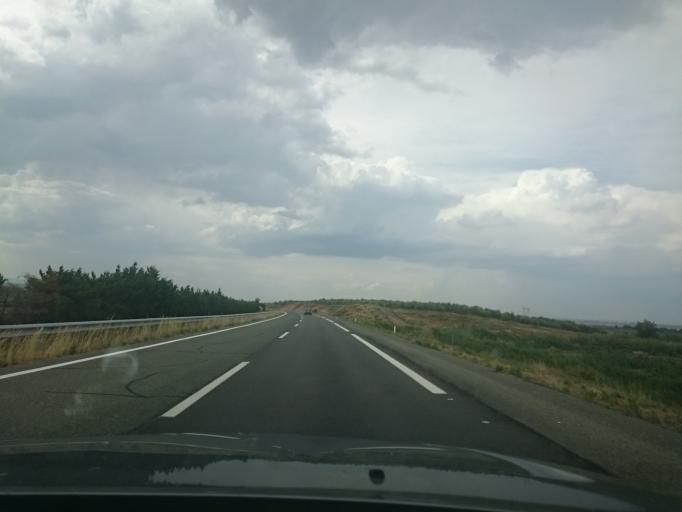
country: ES
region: Navarre
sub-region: Provincia de Navarra
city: Corella
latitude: 42.1442
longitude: -1.7843
